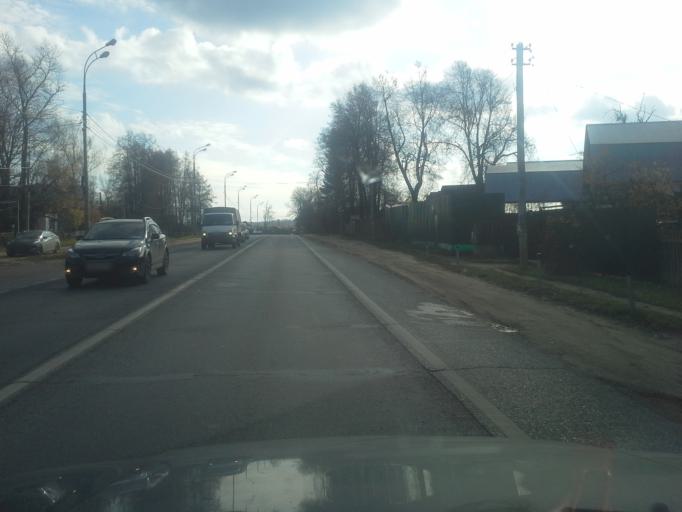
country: RU
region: Moskovskaya
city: Zvenigorod
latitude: 55.6977
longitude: 36.8857
